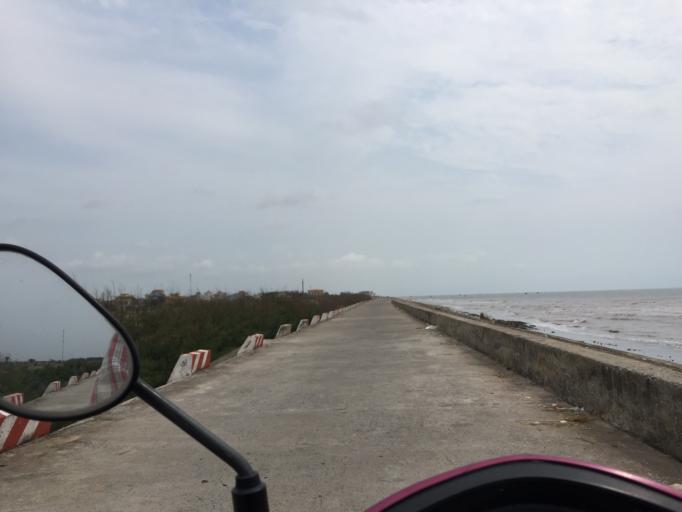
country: VN
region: Ninh Binh
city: Thi Tran Phat Diem
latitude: 20.0166
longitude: 106.2118
